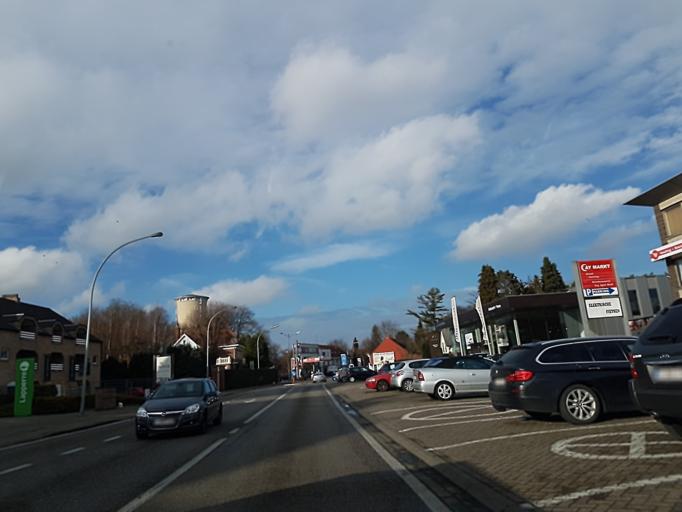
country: BE
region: Flanders
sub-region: Provincie Antwerpen
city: Mol
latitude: 51.1920
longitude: 5.1164
